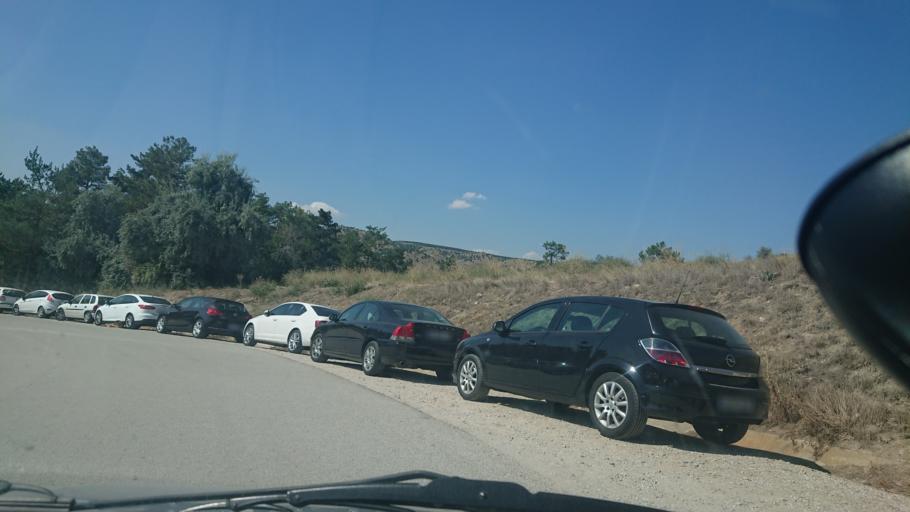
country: TR
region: Ankara
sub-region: Goelbasi
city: Golbasi
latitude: 39.8134
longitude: 32.8220
